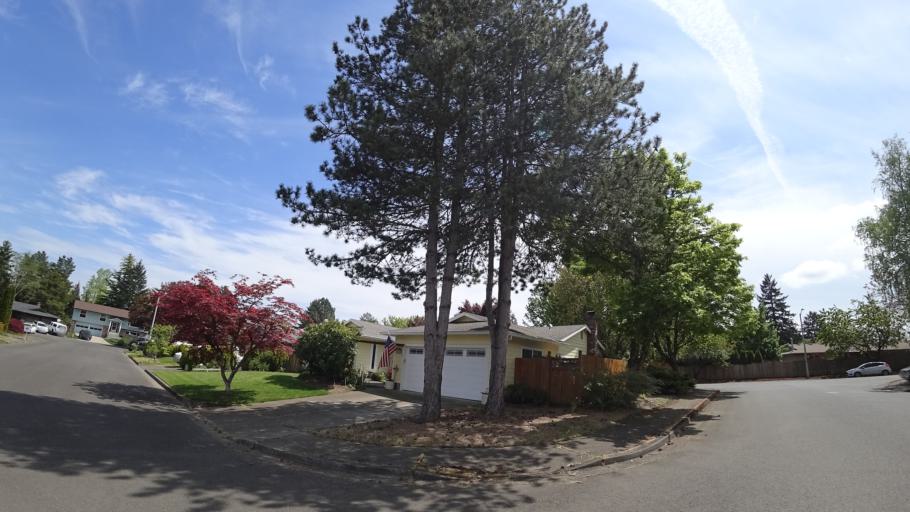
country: US
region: Oregon
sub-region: Washington County
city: Aloha
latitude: 45.4707
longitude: -122.8938
